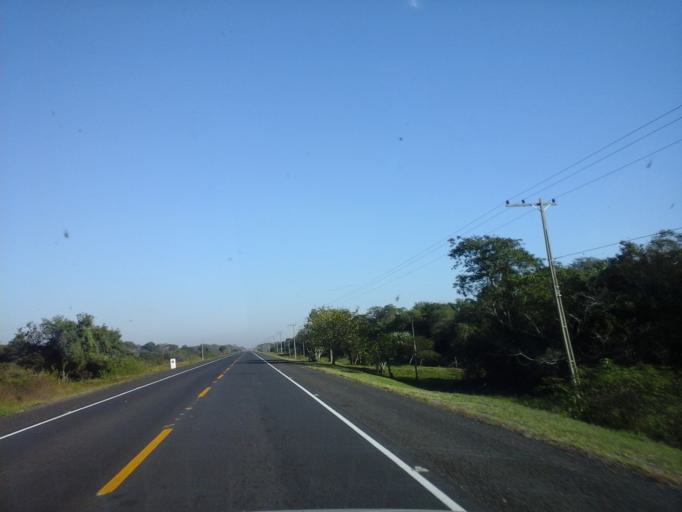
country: PY
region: Neembucu
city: Pilar
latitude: -26.8626
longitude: -58.1617
